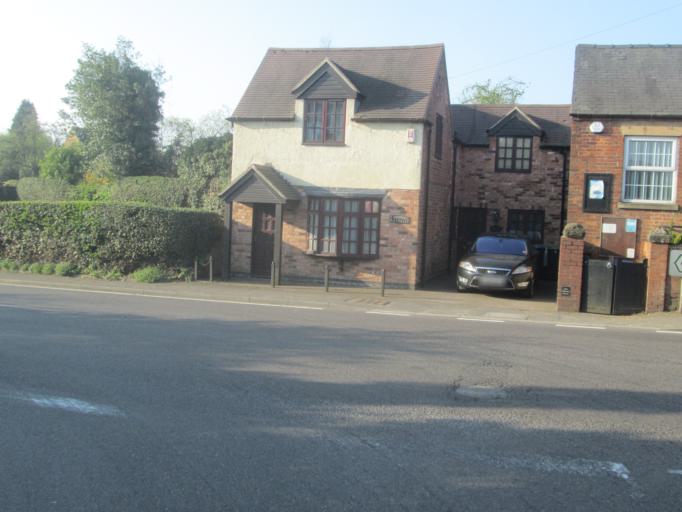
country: GB
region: England
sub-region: Derbyshire
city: Yeldersley
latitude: 52.9707
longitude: -1.6230
